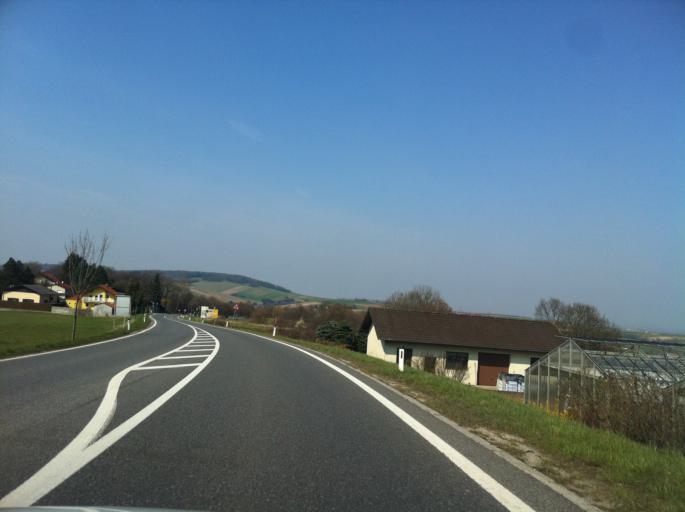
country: AT
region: Lower Austria
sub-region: Politischer Bezirk Tulln
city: Tulbing
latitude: 48.2551
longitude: 16.0878
